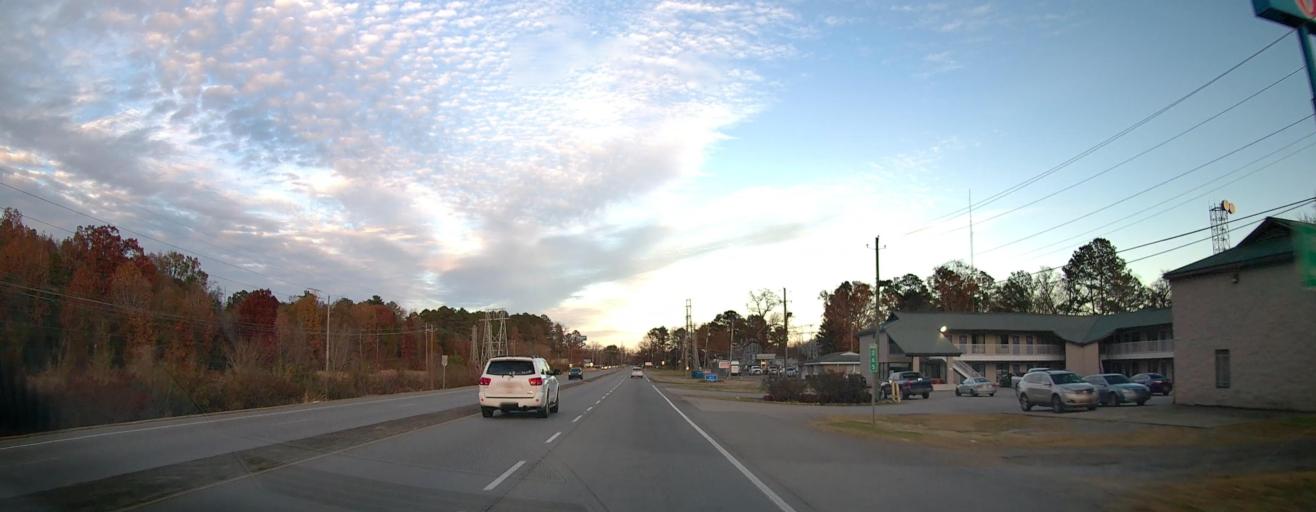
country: US
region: Alabama
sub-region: Etowah County
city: Attalla
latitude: 34.0198
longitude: -86.0706
